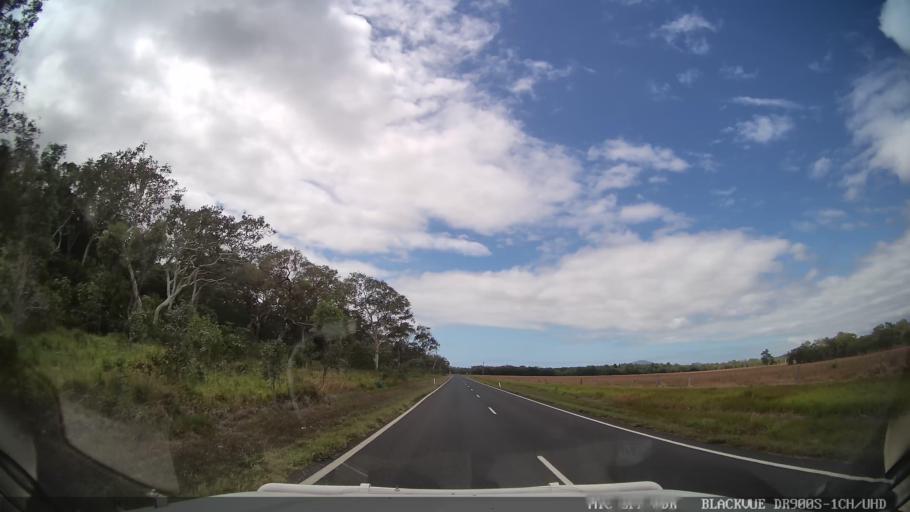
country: AU
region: Queensland
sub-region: Cook
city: Cooktown
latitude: -15.4243
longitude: 145.1487
